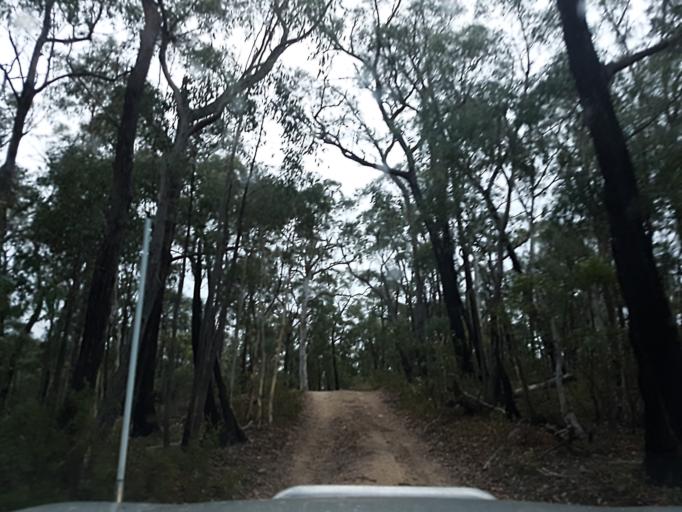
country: AU
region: New South Wales
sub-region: Snowy River
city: Jindabyne
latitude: -36.8507
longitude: 148.2265
